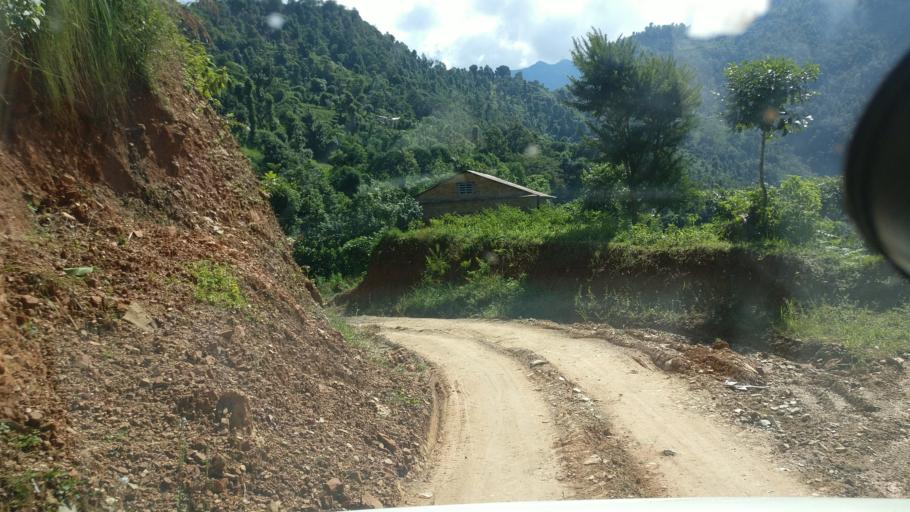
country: NP
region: Western Region
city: Baglung
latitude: 28.1371
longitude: 83.6488
